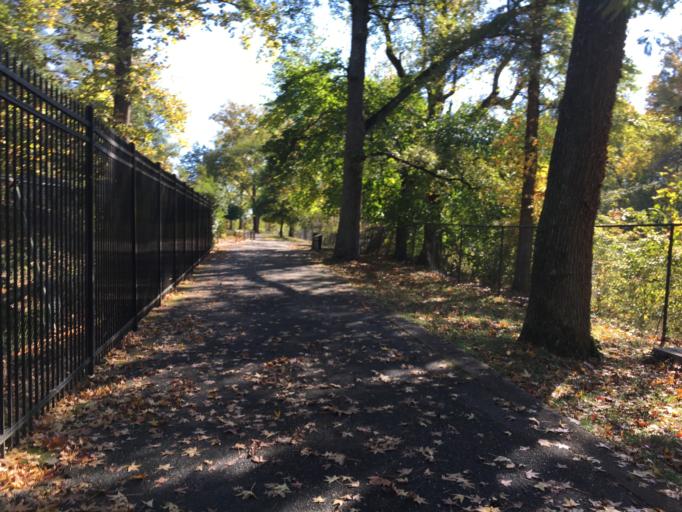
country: US
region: Virginia
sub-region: City of Richmond
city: Richmond
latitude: 37.5339
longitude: -77.4814
